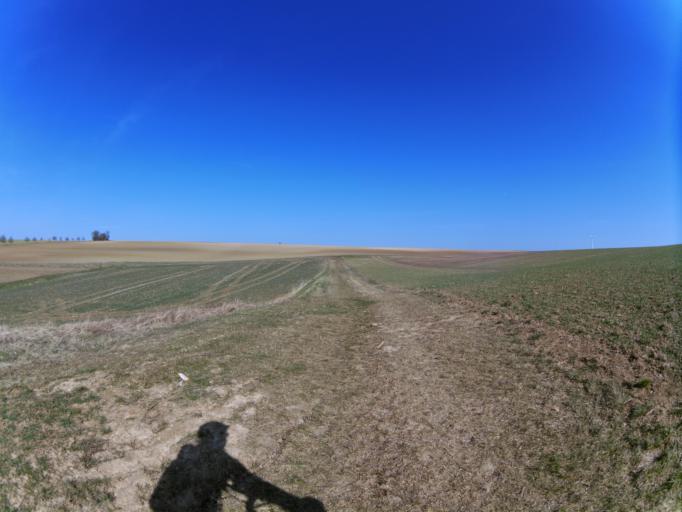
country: DE
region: Bavaria
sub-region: Regierungsbezirk Unterfranken
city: Prosselsheim
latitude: 49.8265
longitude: 10.1279
